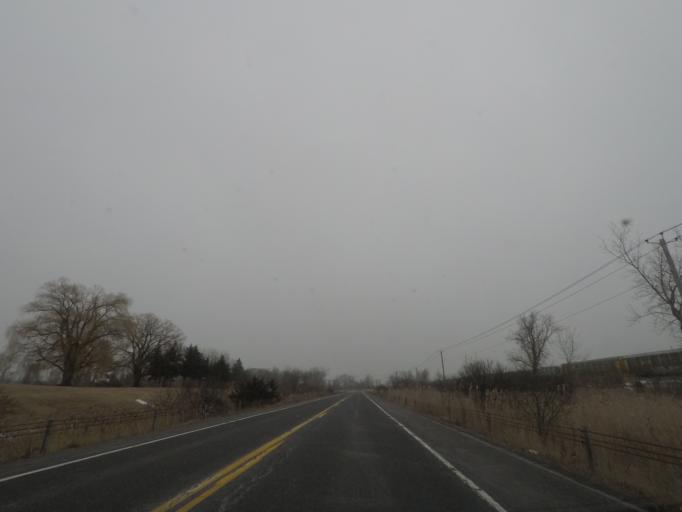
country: US
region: New York
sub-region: Albany County
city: Delmar
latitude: 42.5701
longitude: -73.8550
